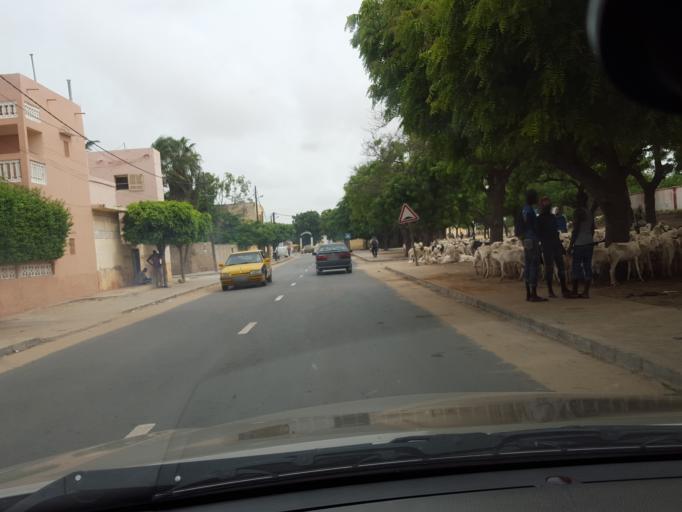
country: SN
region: Saint-Louis
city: Saint-Louis
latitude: 16.0309
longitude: -16.4888
